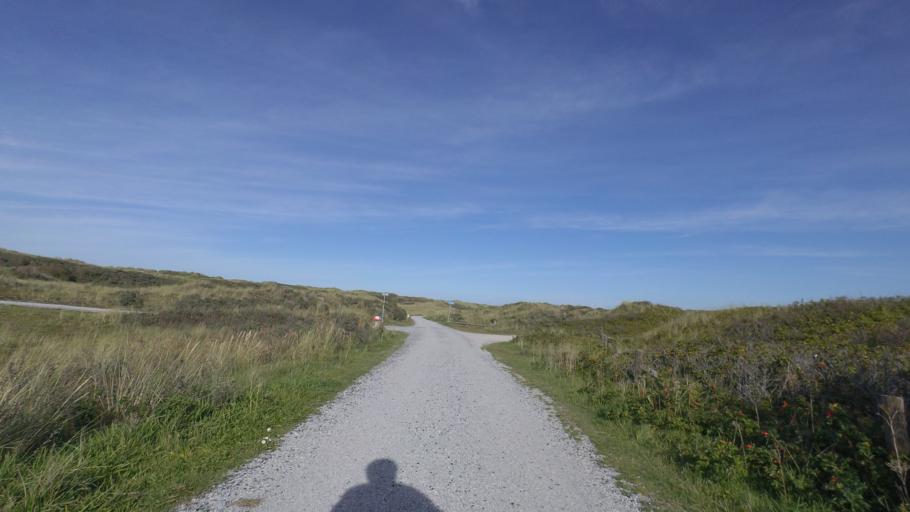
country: NL
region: Friesland
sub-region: Gemeente Ameland
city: Nes
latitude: 53.4600
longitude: 5.8082
